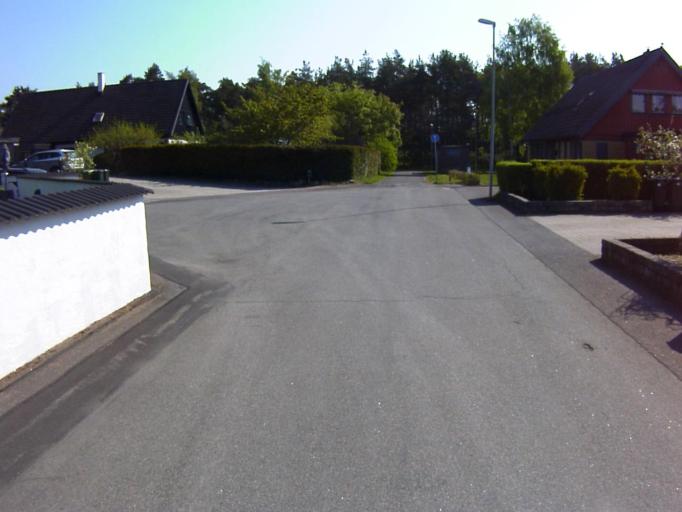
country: SE
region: Skane
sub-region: Kristianstads Kommun
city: Norra Asum
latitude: 55.9495
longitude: 14.1584
